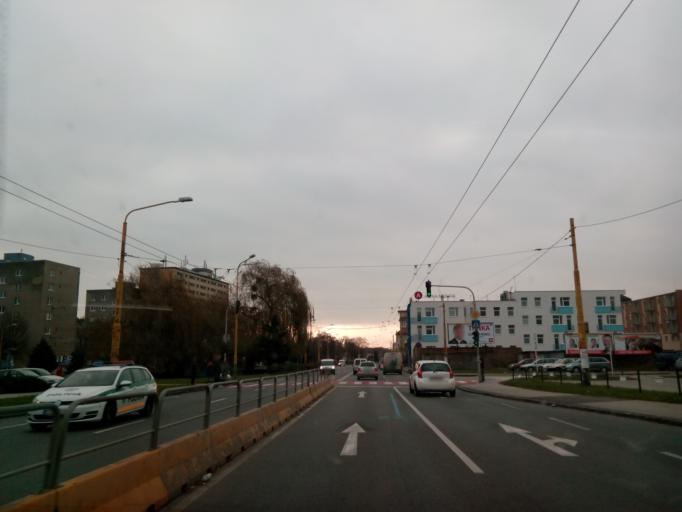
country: SK
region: Kosicky
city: Kosice
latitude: 48.7315
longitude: 21.2543
